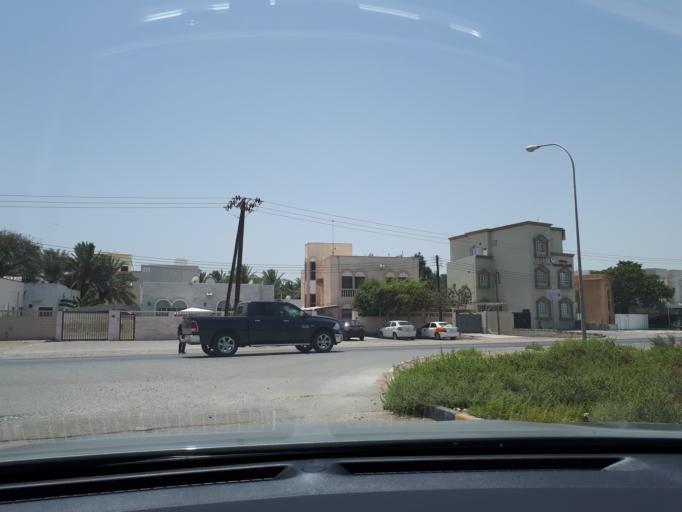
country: OM
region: Muhafazat Masqat
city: As Sib al Jadidah
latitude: 23.6324
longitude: 58.2473
